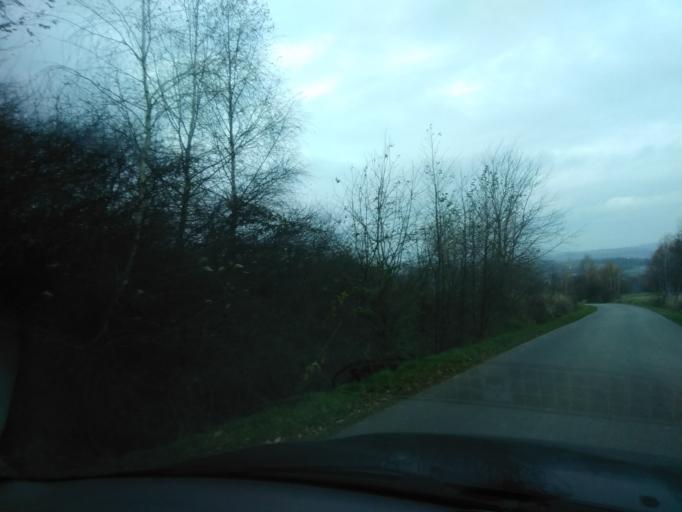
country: PL
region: Subcarpathian Voivodeship
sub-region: Powiat strzyzowski
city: Wysoka Strzyzowska
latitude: 49.8352
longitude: 21.7760
